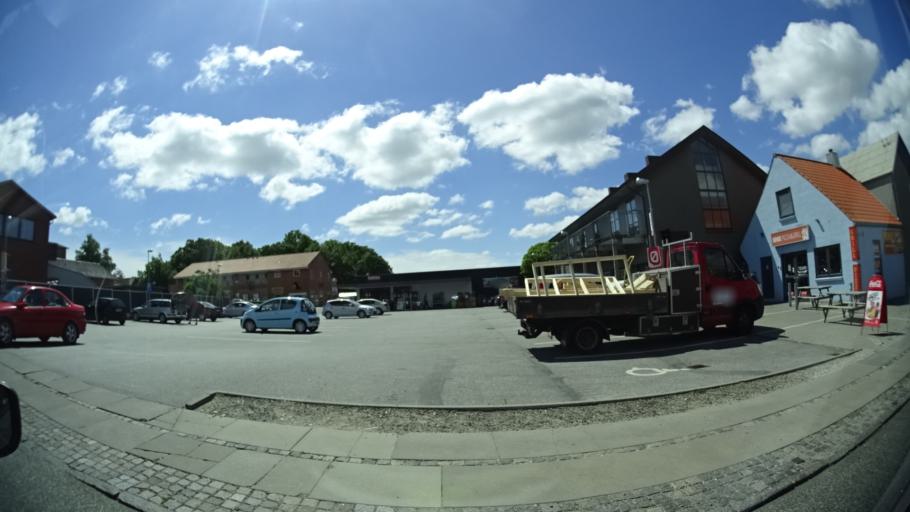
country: DK
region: Central Jutland
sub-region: Syddjurs Kommune
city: Ronde
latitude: 56.3011
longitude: 10.4739
